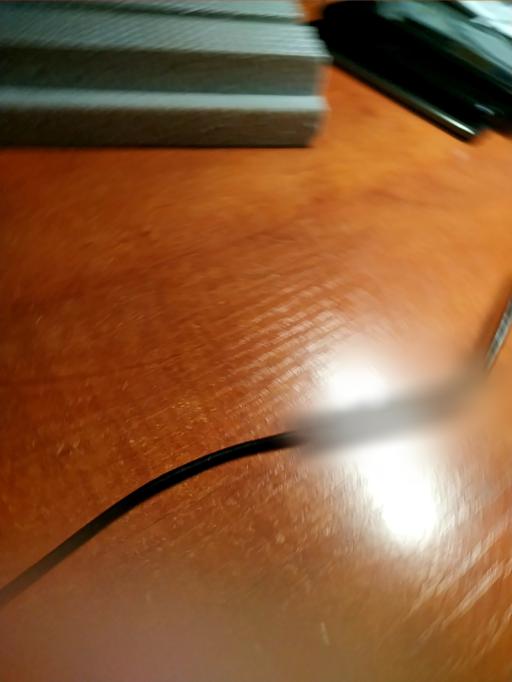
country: RU
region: Tverskaya
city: Staraya Toropa
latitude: 56.3471
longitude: 31.8280
